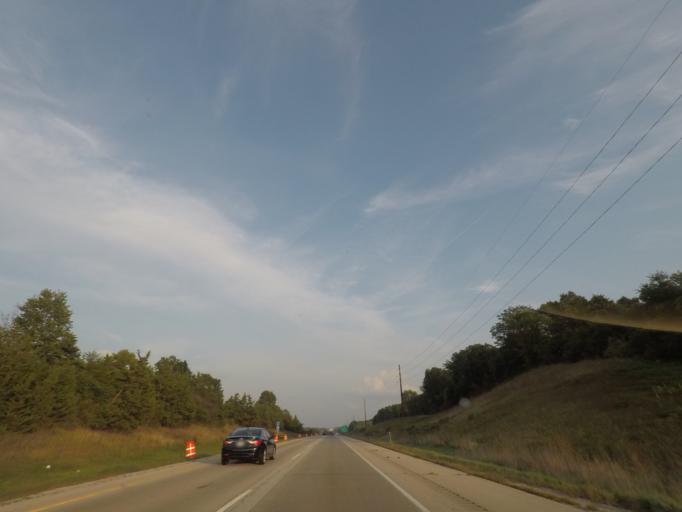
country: US
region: Wisconsin
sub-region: Jefferson County
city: Lake Mills
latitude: 43.1020
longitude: -88.9347
